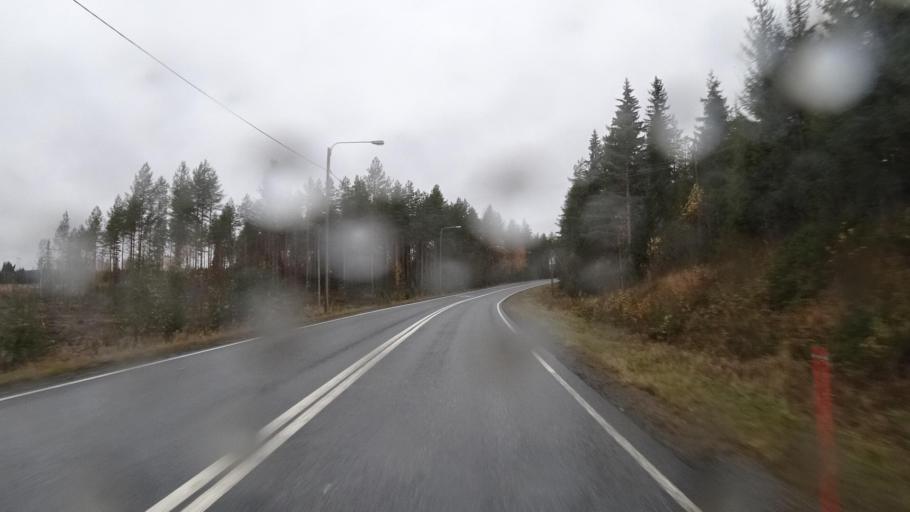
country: FI
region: Northern Savo
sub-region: Koillis-Savo
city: Tuusniemi
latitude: 62.8721
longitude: 28.3167
